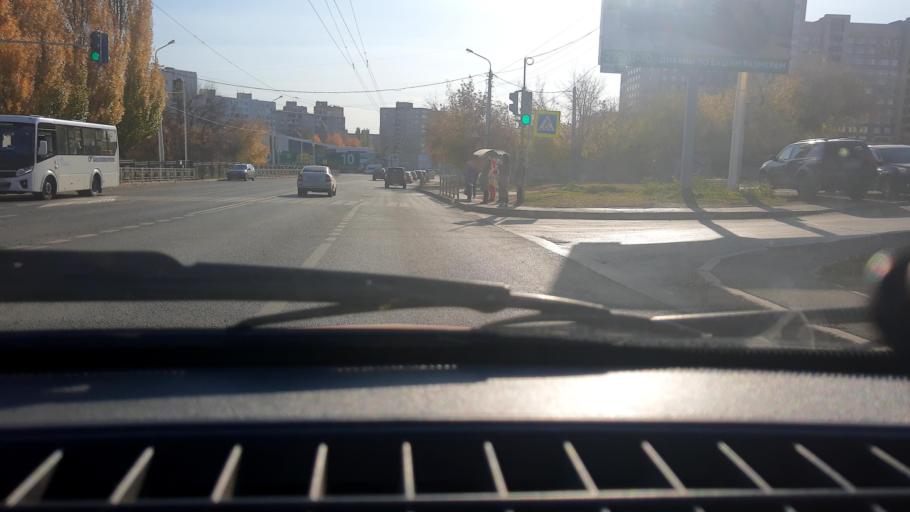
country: RU
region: Bashkortostan
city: Ufa
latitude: 54.6994
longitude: 55.9949
